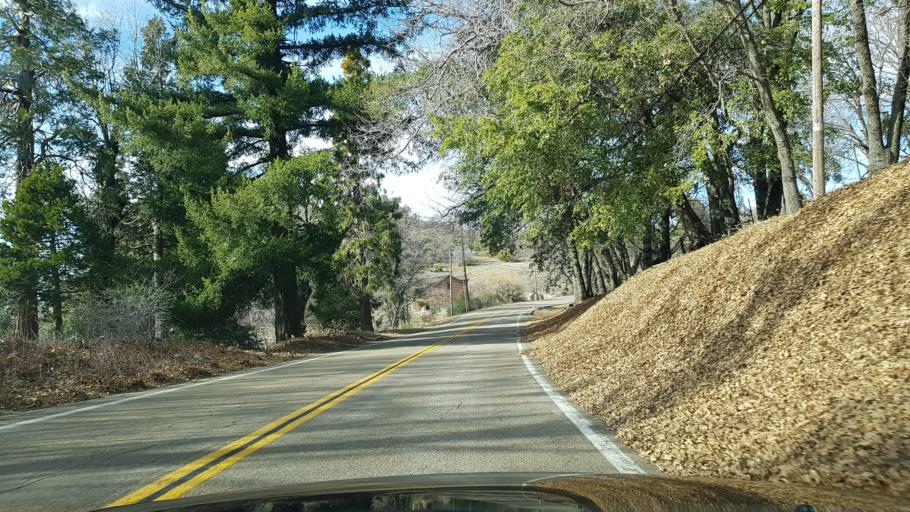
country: US
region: California
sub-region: Riverside County
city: Aguanga
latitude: 33.3204
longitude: -116.8912
